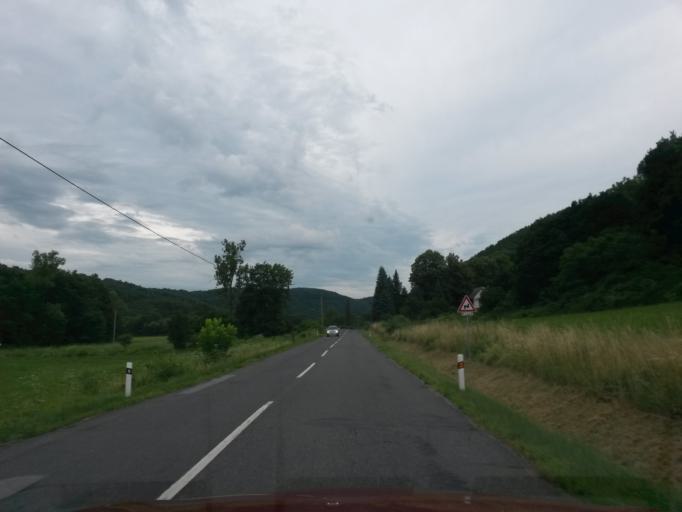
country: SK
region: Banskobystricky
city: Velky Krtis
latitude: 48.3395
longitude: 19.4088
